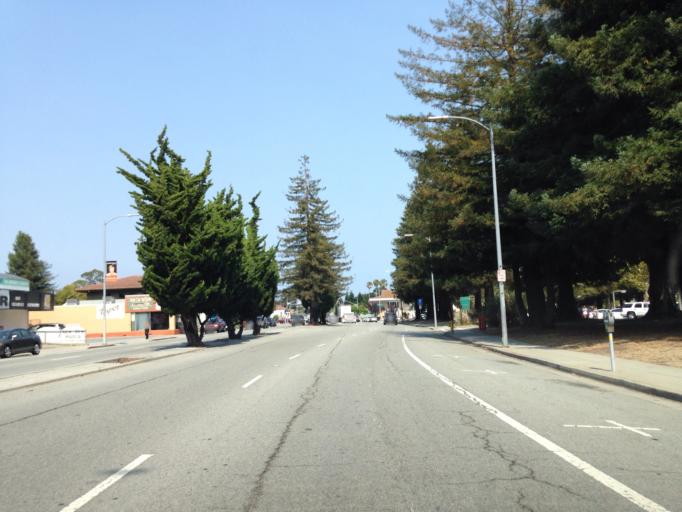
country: US
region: California
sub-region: Santa Cruz County
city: Santa Cruz
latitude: 36.9789
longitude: -122.0233
